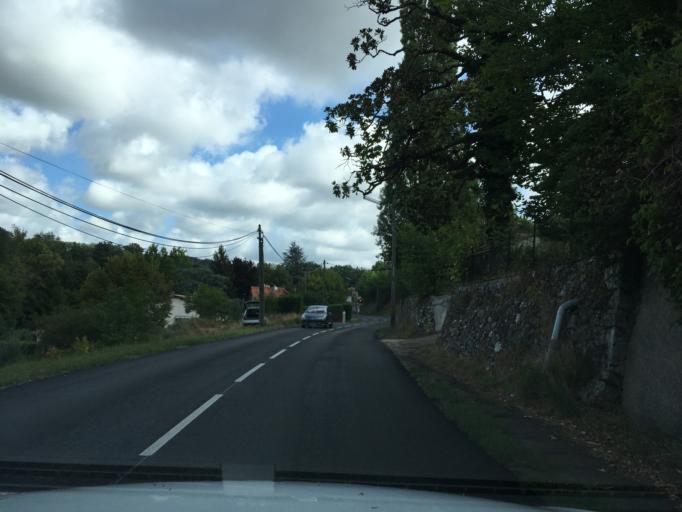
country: FR
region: Aquitaine
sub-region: Departement du Lot-et-Garonne
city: Le Passage
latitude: 44.2200
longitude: 0.6127
